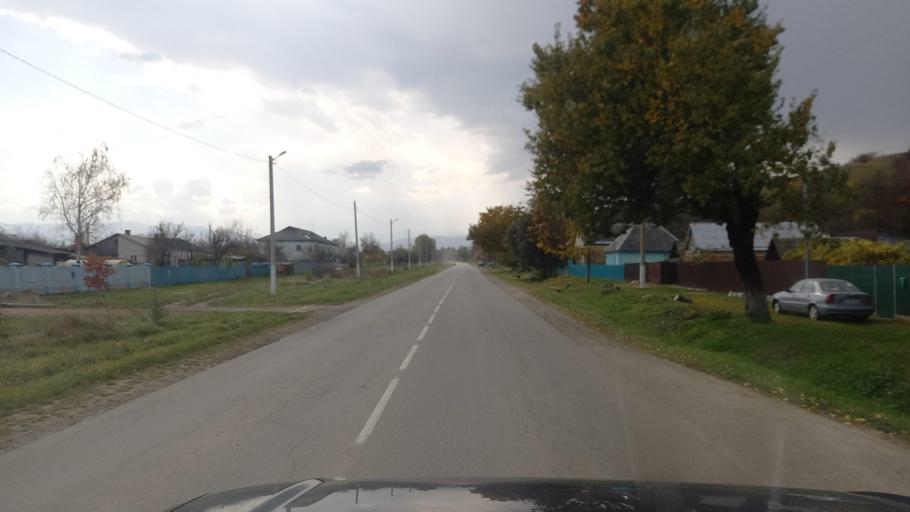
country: RU
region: Krasnodarskiy
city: Psebay
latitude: 44.1383
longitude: 40.8189
